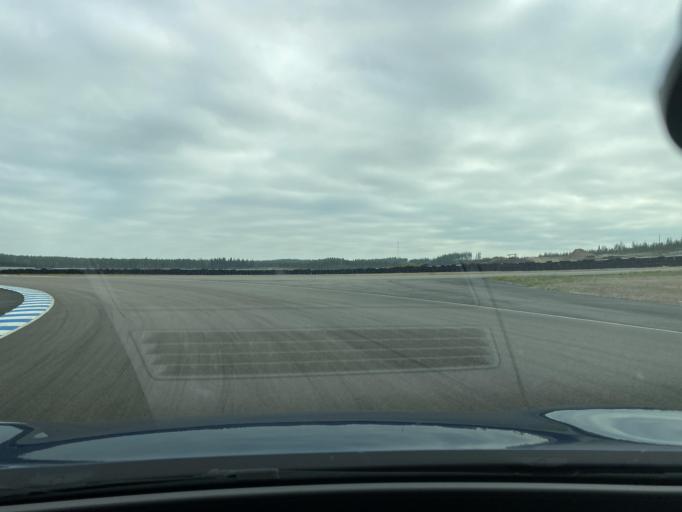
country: FI
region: Kymenlaakso
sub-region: Kouvola
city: Iitti
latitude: 60.8798
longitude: 26.4779
